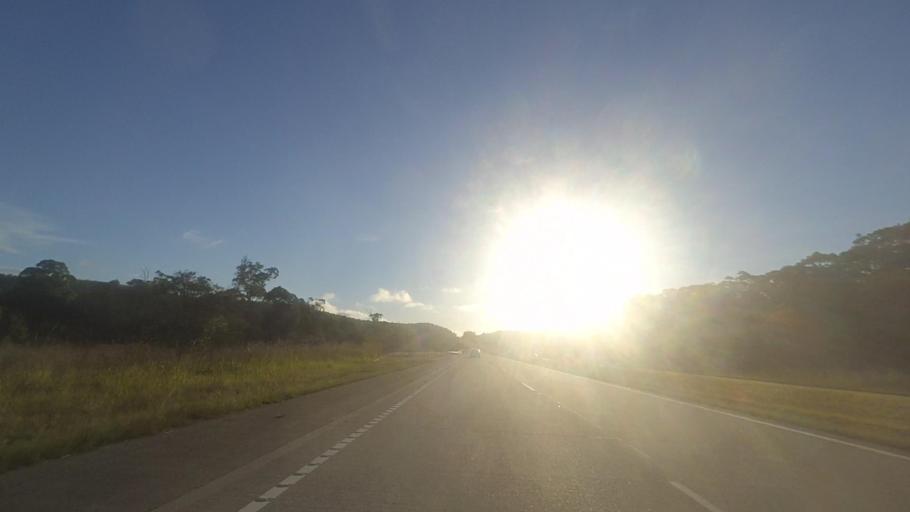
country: AU
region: New South Wales
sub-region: Great Lakes
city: Bulahdelah
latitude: -32.5276
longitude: 152.1913
